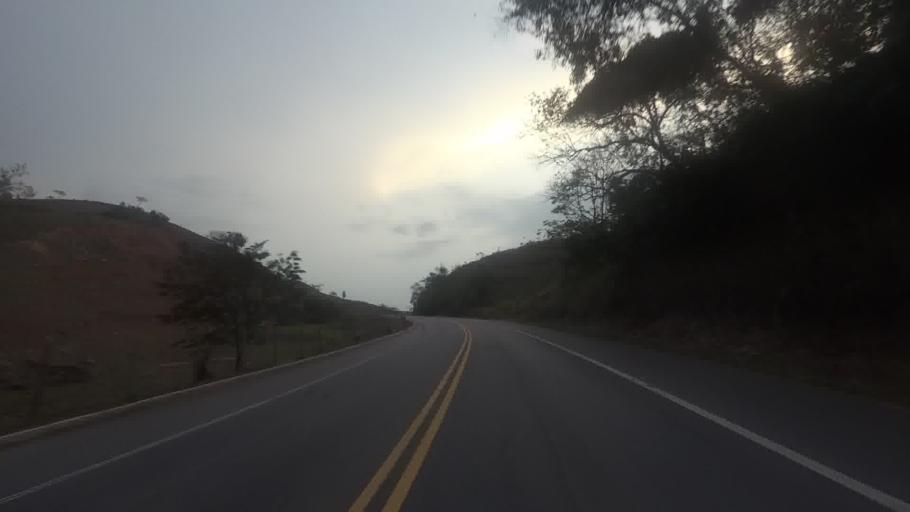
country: BR
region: Minas Gerais
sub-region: Alem Paraiba
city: Alem Paraiba
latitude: -21.8425
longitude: -42.6284
